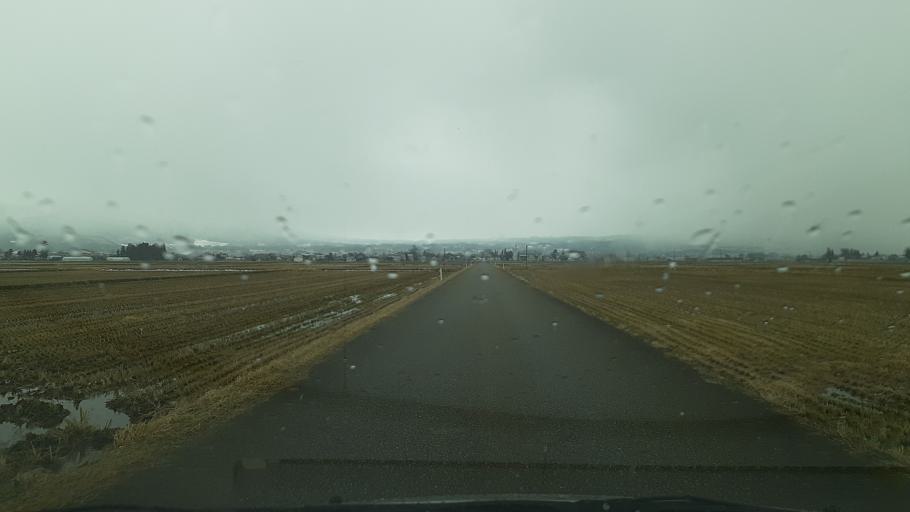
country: JP
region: Fukushima
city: Kitakata
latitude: 37.5606
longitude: 139.8745
